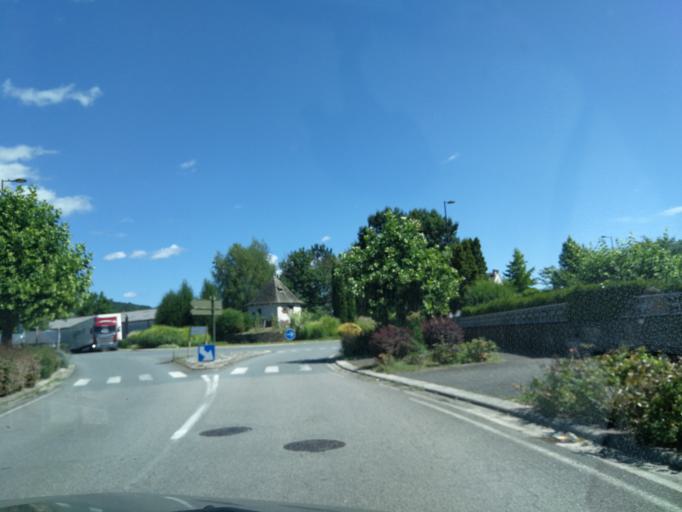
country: FR
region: Limousin
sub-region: Departement de la Correze
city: Argentat
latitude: 45.0917
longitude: 1.9314
